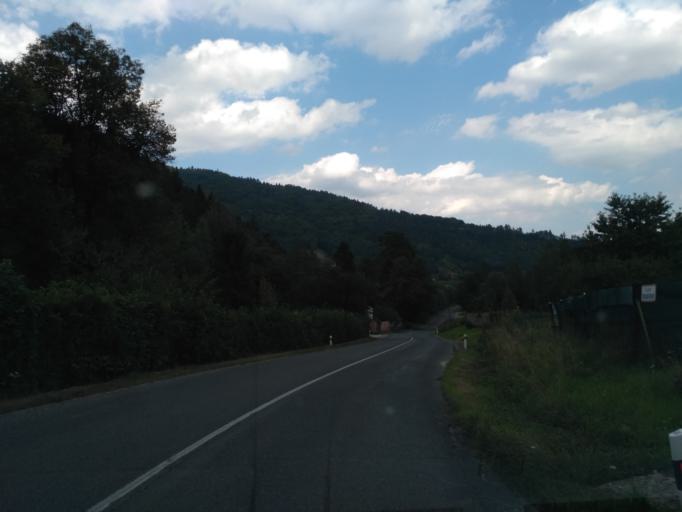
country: SK
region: Kosicky
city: Gelnica
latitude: 48.8648
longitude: 20.9575
